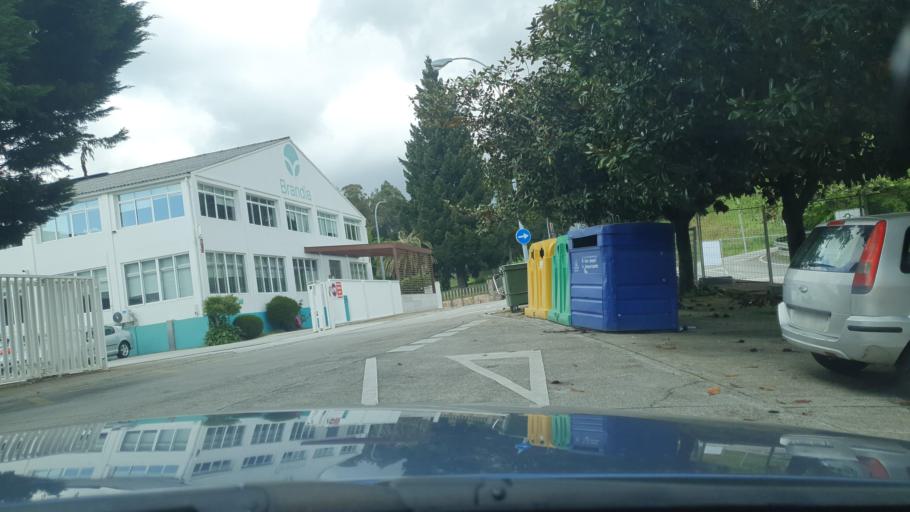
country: ES
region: Galicia
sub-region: Provincia da Coruna
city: Santiago de Compostela
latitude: 42.8721
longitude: -8.5806
